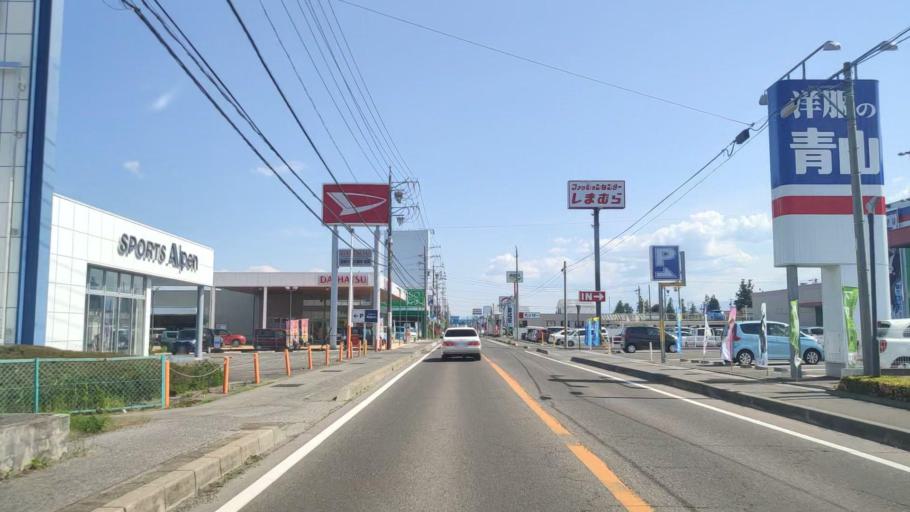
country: JP
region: Nagano
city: Hotaka
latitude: 36.3282
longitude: 137.8923
